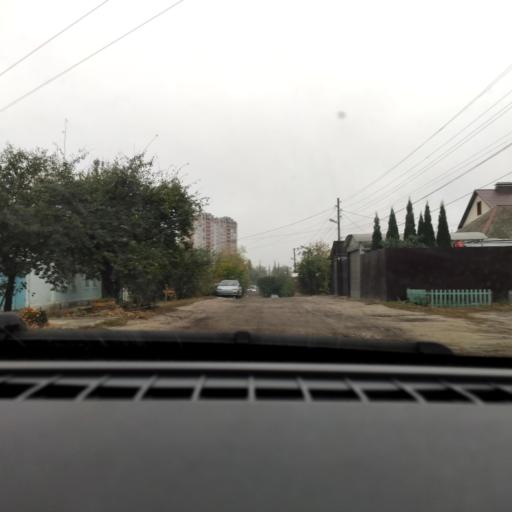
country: RU
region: Voronezj
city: Voronezh
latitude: 51.6653
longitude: 39.2845
